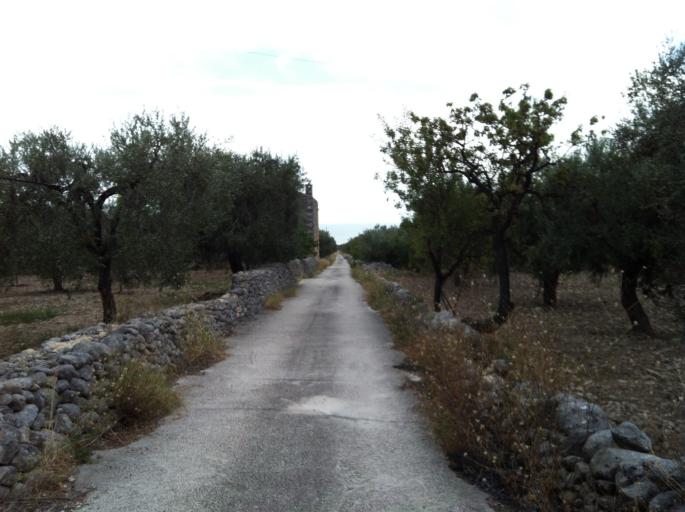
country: IT
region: Apulia
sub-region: Provincia di Foggia
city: Monte Sant'Angelo
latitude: 41.6583
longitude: 15.9546
